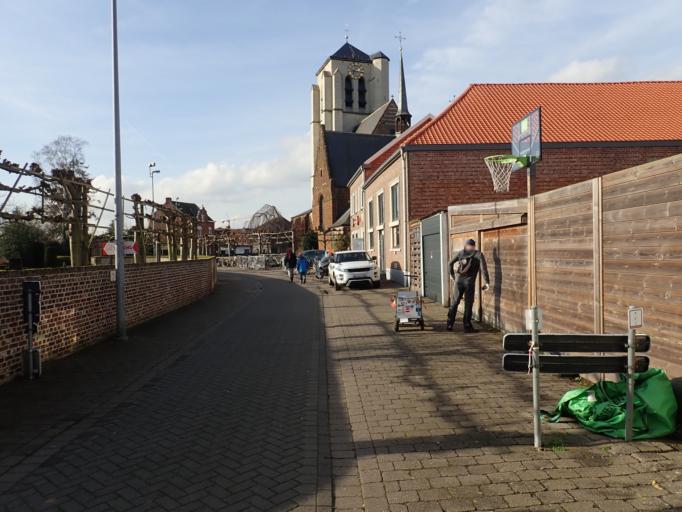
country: BE
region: Flanders
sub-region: Provincie Vlaams-Brabant
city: Holsbeek
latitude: 50.9472
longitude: 4.7571
